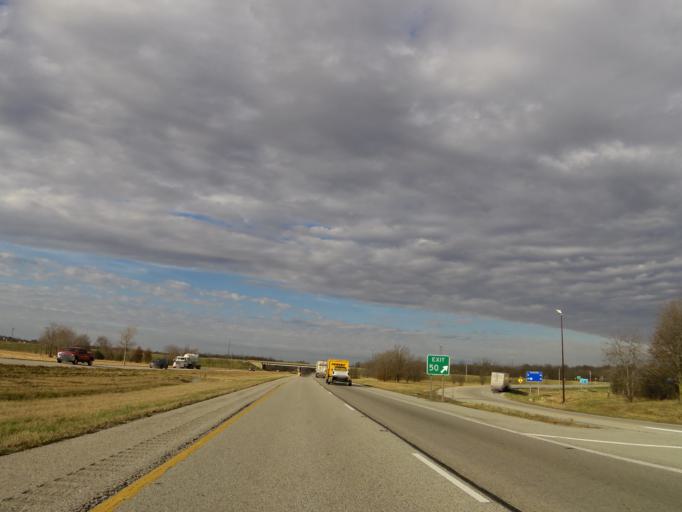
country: US
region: Illinois
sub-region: Washington County
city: Nashville
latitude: 38.3913
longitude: -89.3666
